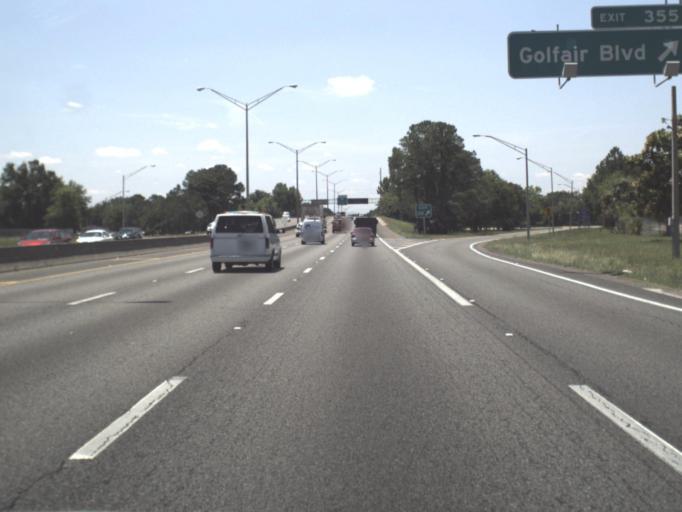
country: US
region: Florida
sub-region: Duval County
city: Jacksonville
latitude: 30.3685
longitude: -81.6690
